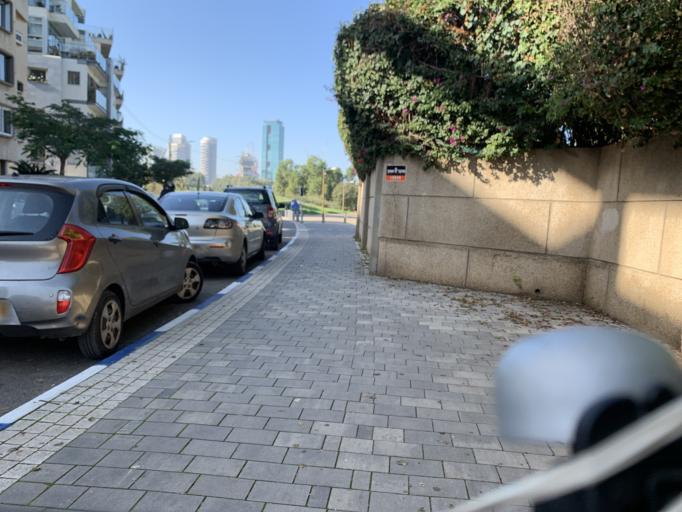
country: IL
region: Tel Aviv
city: Ramat Gan
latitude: 32.0952
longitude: 34.8103
